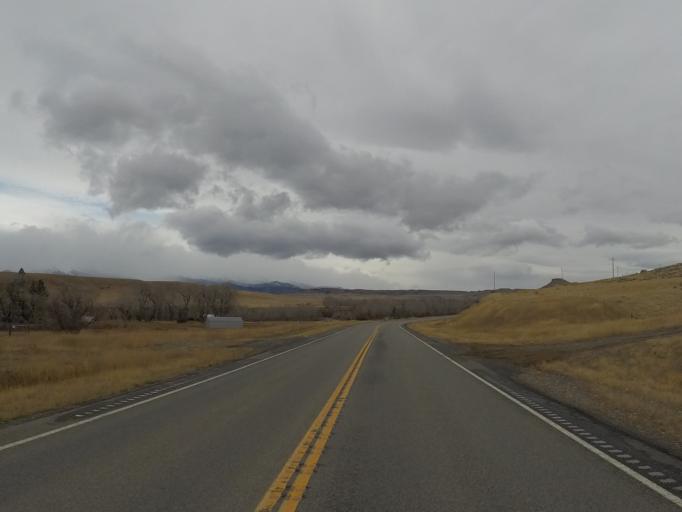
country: US
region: Montana
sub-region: Sweet Grass County
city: Big Timber
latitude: 45.9268
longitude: -109.9831
